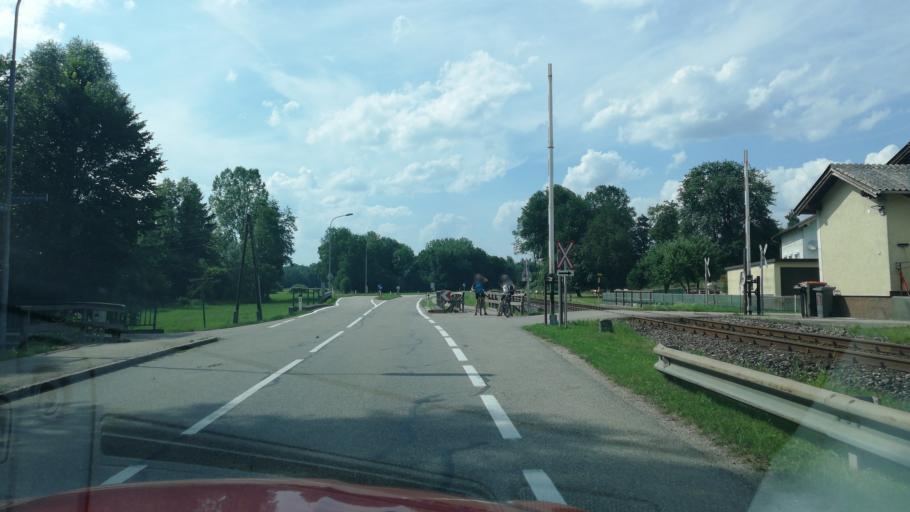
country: AT
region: Upper Austria
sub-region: Politischer Bezirk Vocklabruck
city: Puhret
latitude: 48.0235
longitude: 13.7096
